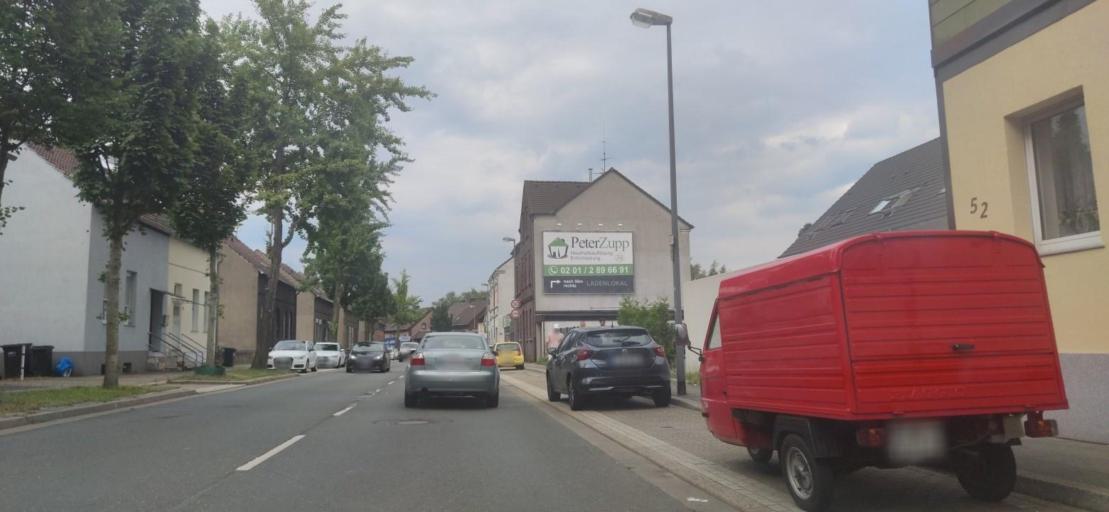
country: DE
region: North Rhine-Westphalia
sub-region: Regierungsbezirk Dusseldorf
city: Essen
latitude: 51.5065
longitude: 7.0494
